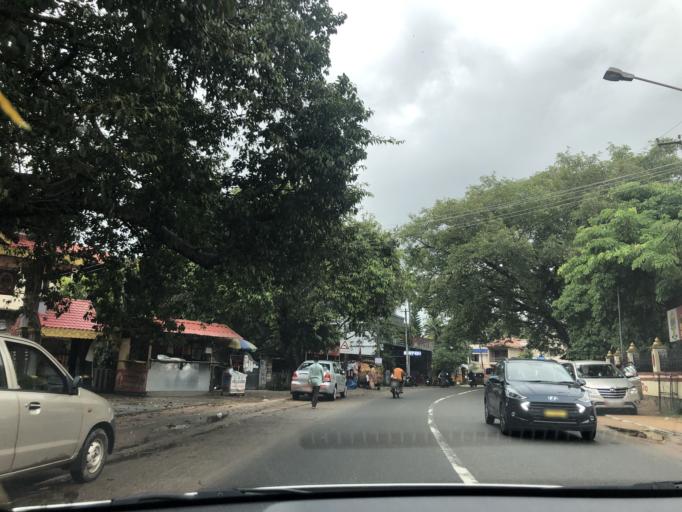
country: IN
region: Kerala
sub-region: Thiruvananthapuram
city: Thiruvananthapuram
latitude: 8.5112
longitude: 76.9080
